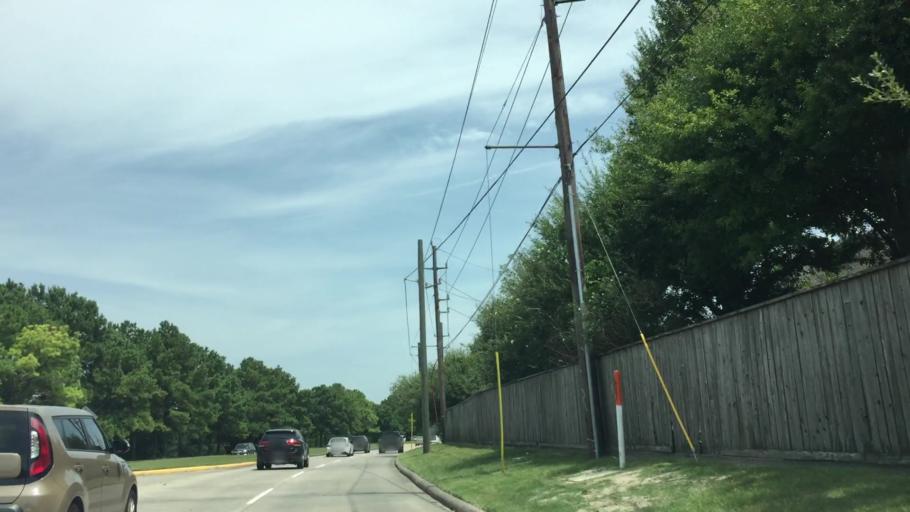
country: US
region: Texas
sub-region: Harris County
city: Jersey Village
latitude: 29.9088
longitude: -95.5641
